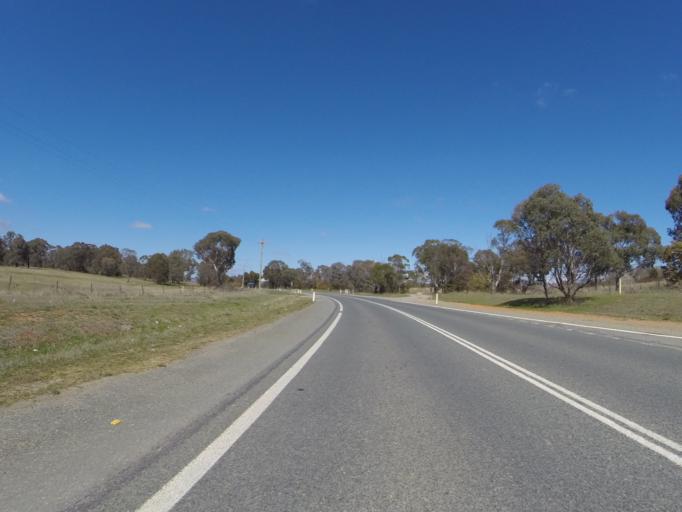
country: AU
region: New South Wales
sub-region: Queanbeyan
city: Queanbeyan
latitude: -35.3266
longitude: 149.2386
